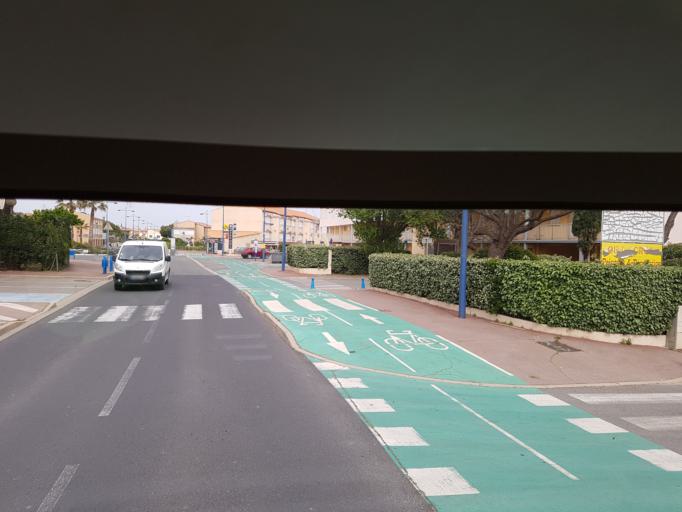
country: FR
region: Languedoc-Roussillon
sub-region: Departement de l'Aude
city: Fleury
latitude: 43.1750
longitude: 3.1853
